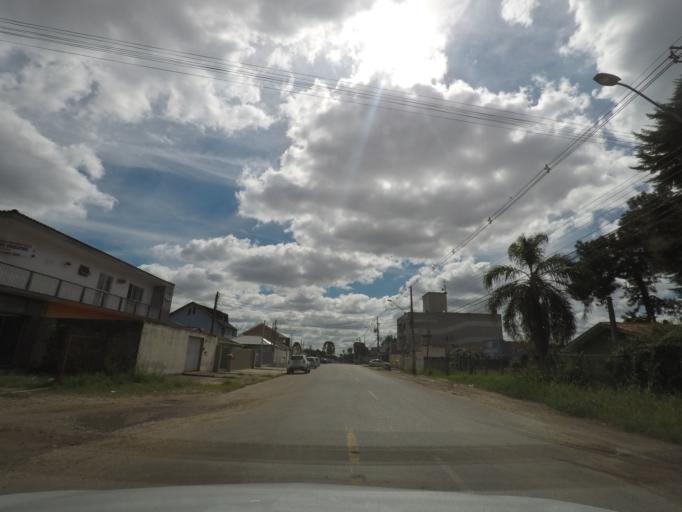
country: BR
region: Parana
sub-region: Sao Jose Dos Pinhais
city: Sao Jose dos Pinhais
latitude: -25.4943
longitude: -49.2370
